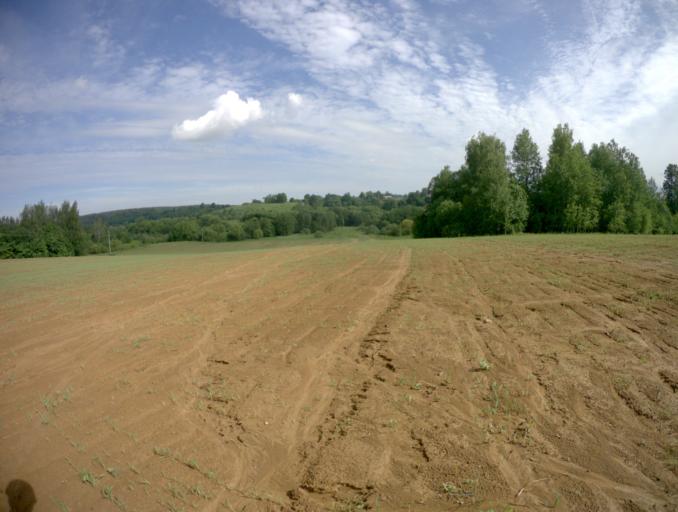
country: RU
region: Vladimir
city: Lakinsk
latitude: 56.0997
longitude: 39.9196
